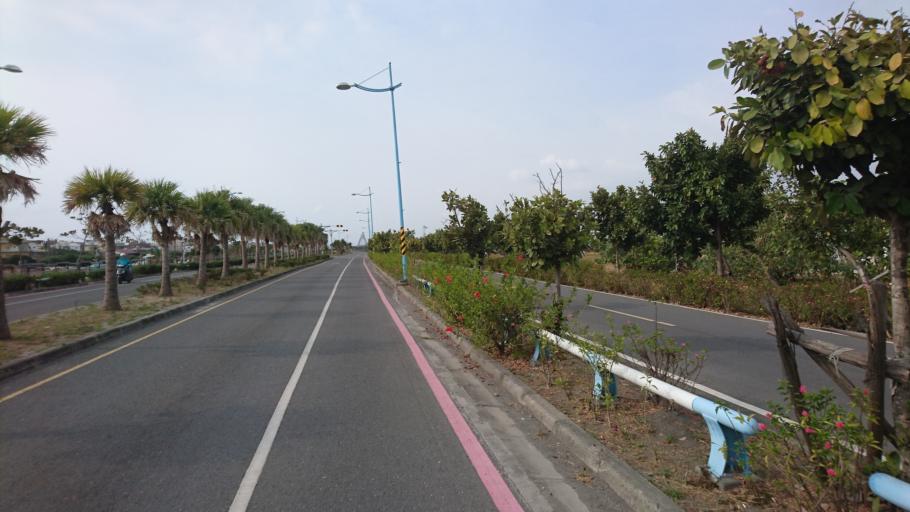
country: TW
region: Taiwan
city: Fengshan
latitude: 22.4382
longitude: 120.4737
